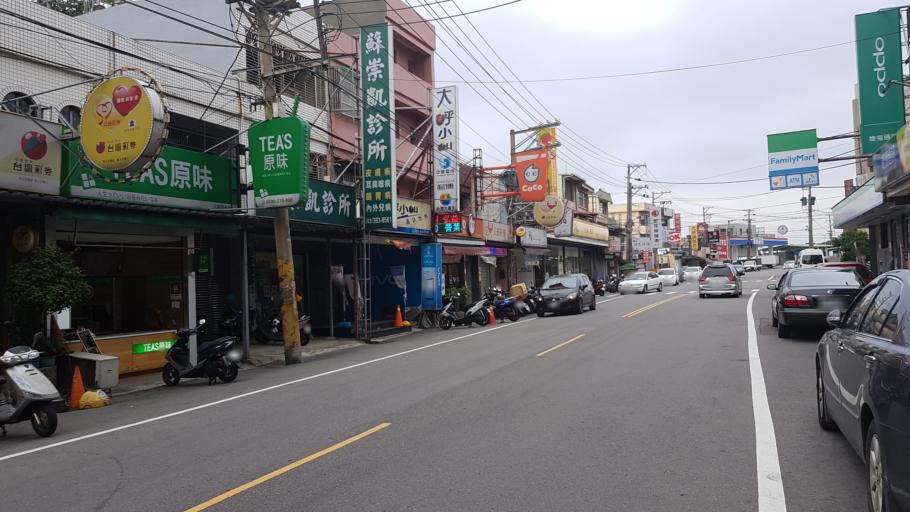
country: TW
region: Taiwan
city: Taoyuan City
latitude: 25.0748
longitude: 121.2590
